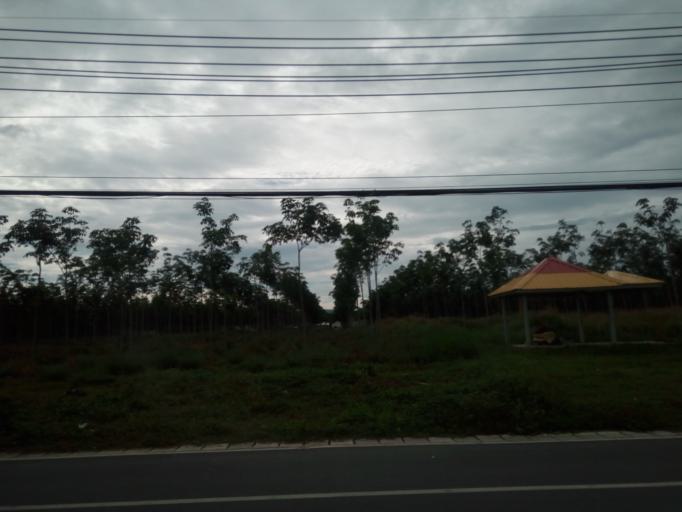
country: TH
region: Phuket
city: Mueang Phuket
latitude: 7.8522
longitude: 98.3812
